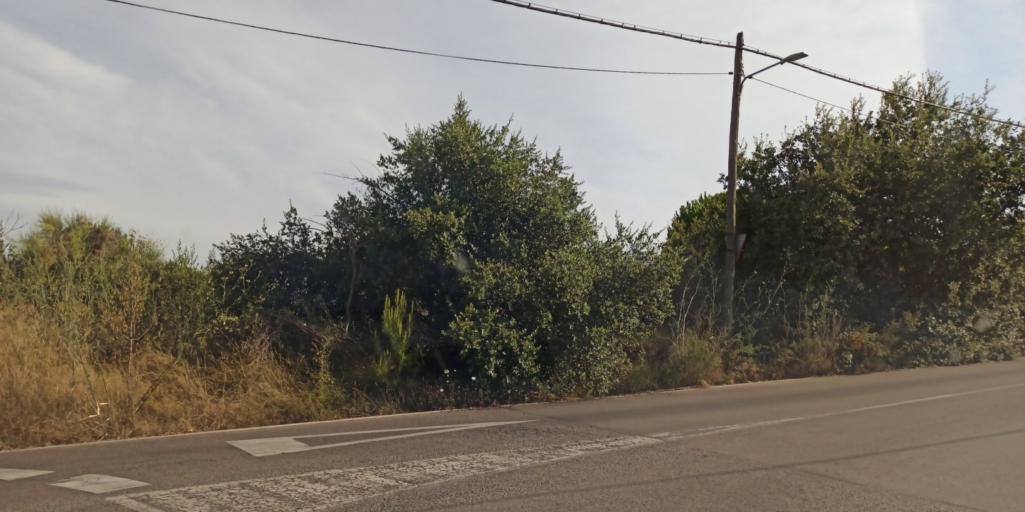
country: ES
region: Catalonia
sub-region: Provincia de Barcelona
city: Santa Coloma de Cervello
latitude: 41.3597
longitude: 2.0252
